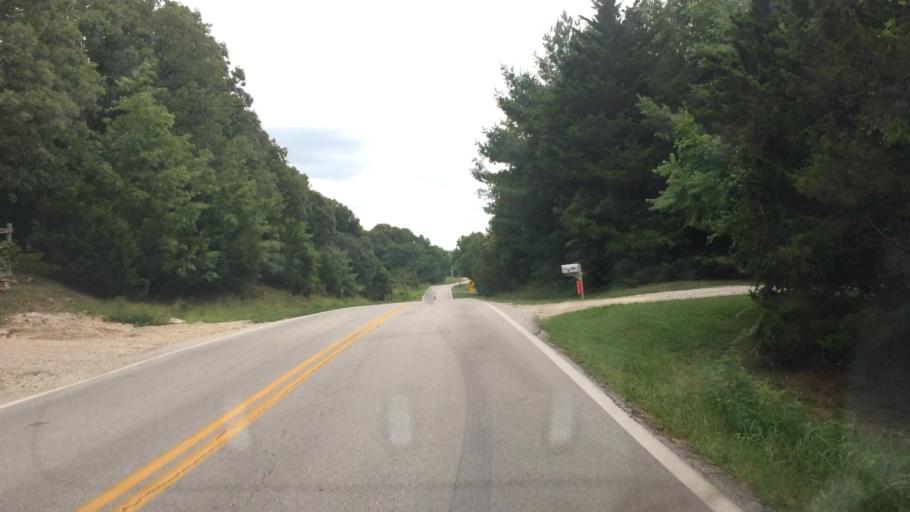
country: US
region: Missouri
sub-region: Greene County
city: Strafford
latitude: 37.2978
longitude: -93.0832
